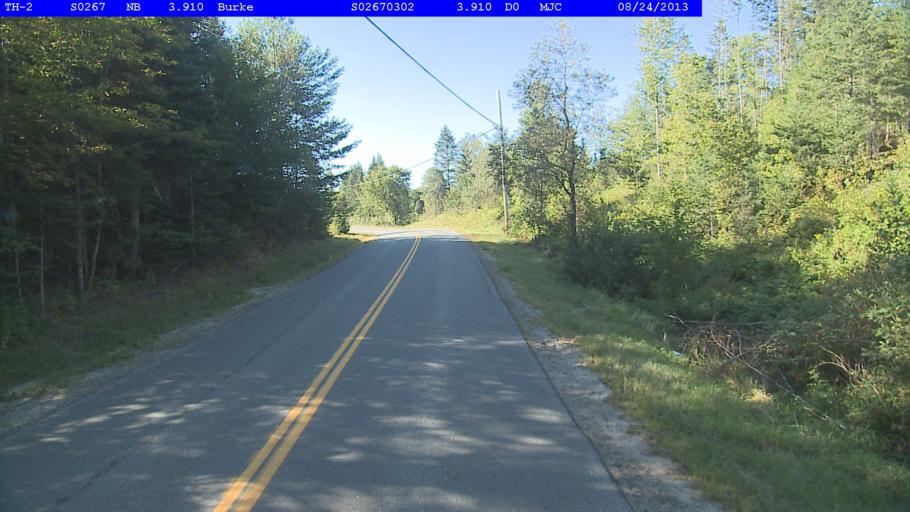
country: US
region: Vermont
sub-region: Caledonia County
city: Lyndonville
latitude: 44.6315
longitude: -71.9658
